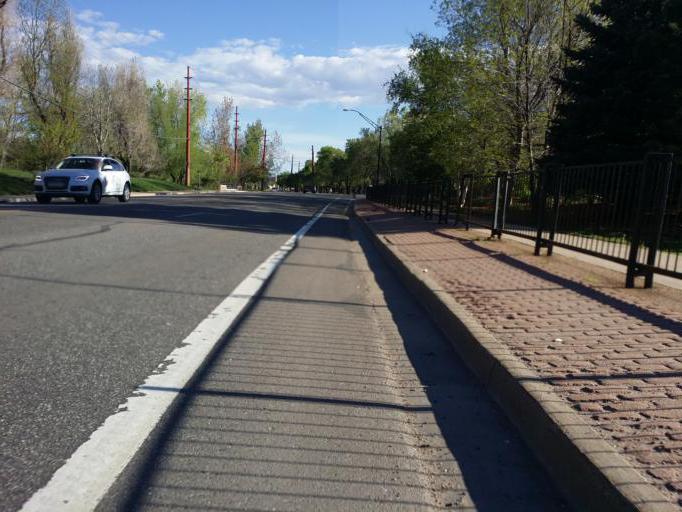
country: US
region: Colorado
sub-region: Boulder County
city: Boulder
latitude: 40.0103
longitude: -105.2535
